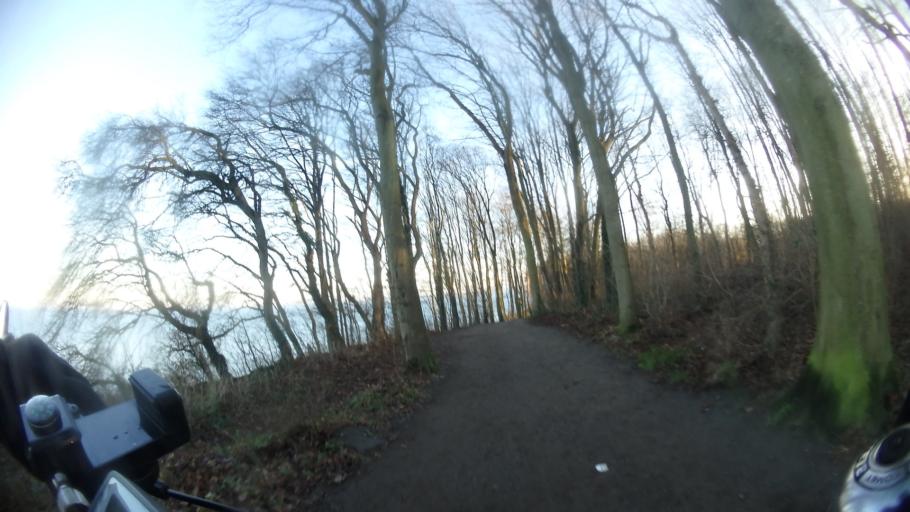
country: DE
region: Schleswig-Holstein
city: Travemuende
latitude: 53.9876
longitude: 10.8747
